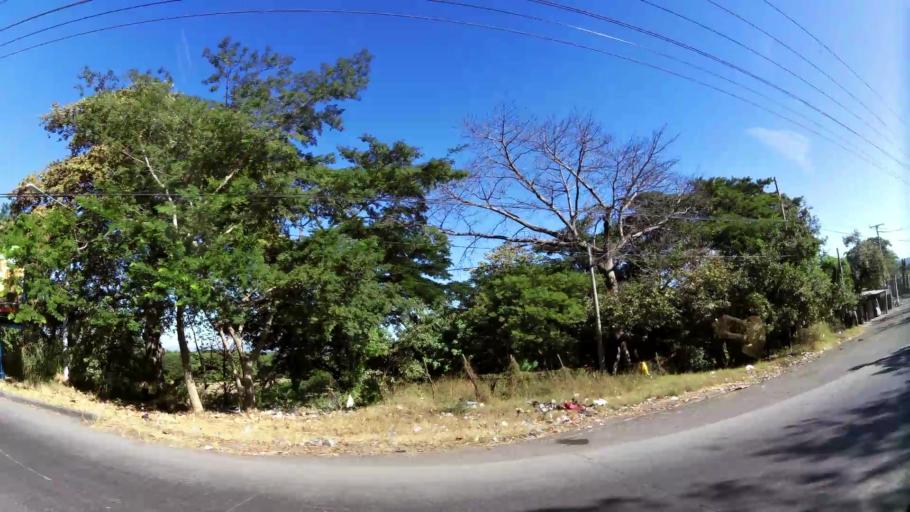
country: SV
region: San Miguel
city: San Miguel
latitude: 13.4590
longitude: -88.1573
